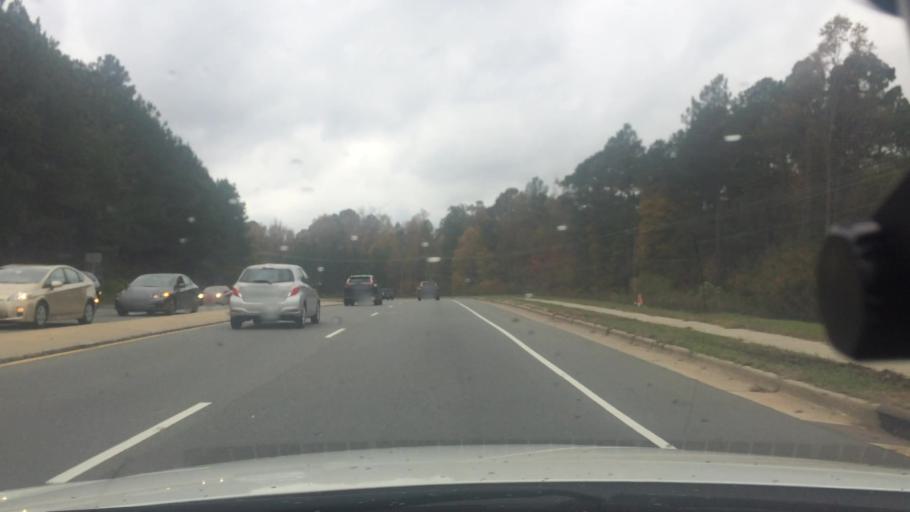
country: US
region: North Carolina
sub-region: Orange County
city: Chapel Hill
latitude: 35.8912
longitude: -79.0597
